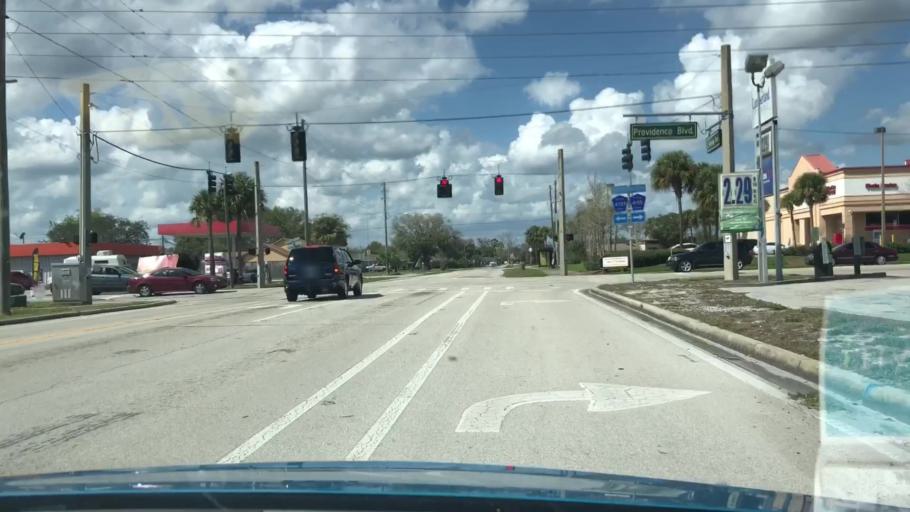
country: US
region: Florida
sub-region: Volusia County
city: Deltona
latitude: 28.8837
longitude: -81.2395
